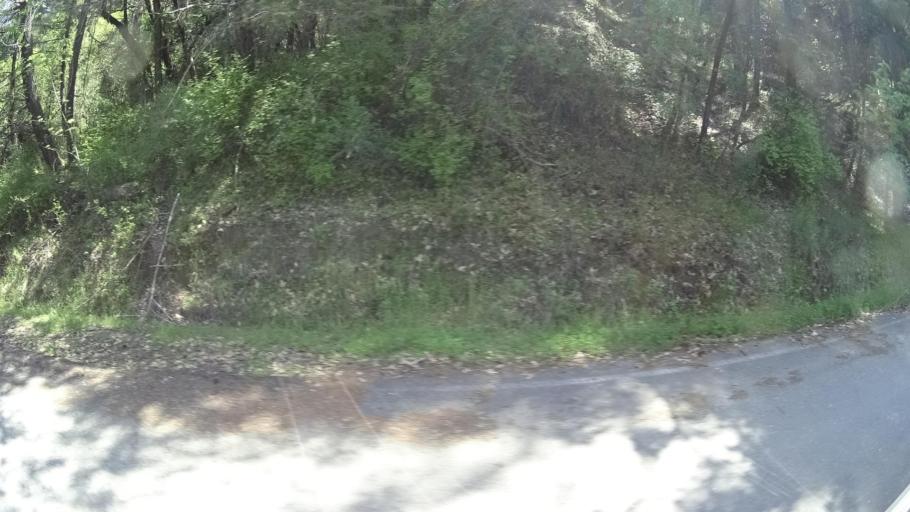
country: US
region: California
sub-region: Humboldt County
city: Redway
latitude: 40.1998
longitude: -123.5196
